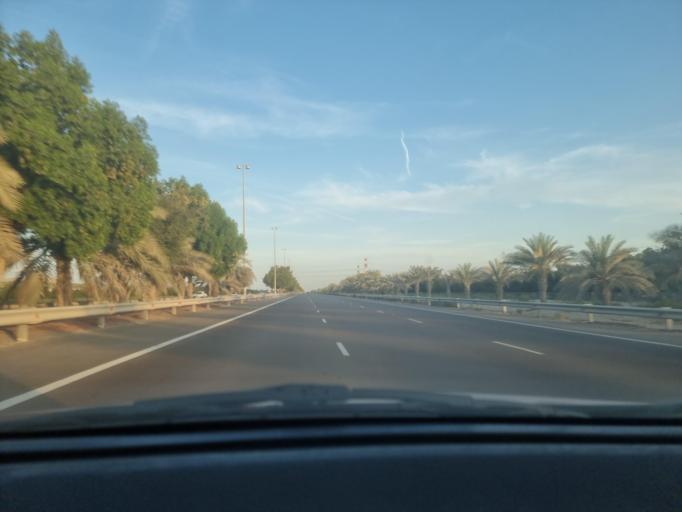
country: AE
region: Abu Dhabi
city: Abu Dhabi
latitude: 24.2289
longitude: 54.7834
